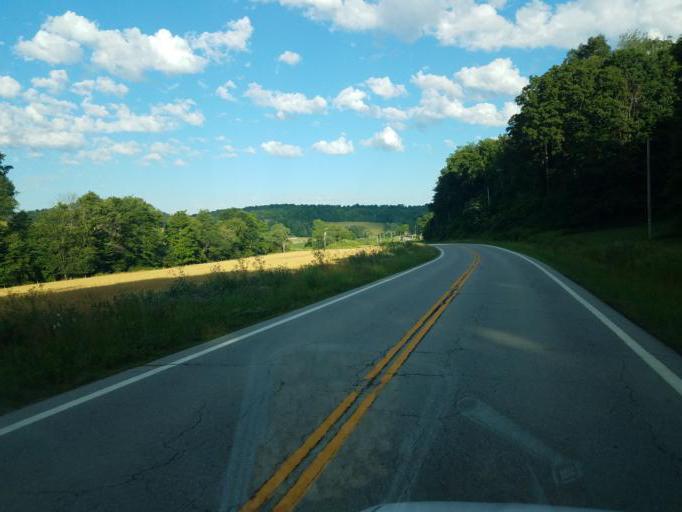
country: US
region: Ohio
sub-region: Sandusky County
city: Bellville
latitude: 40.5798
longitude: -82.4055
